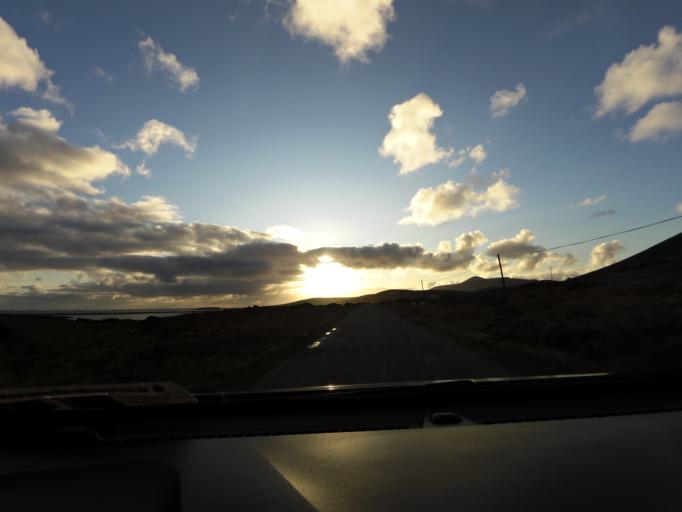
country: IE
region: Connaught
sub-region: Maigh Eo
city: Belmullet
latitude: 53.9975
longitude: -10.0479
